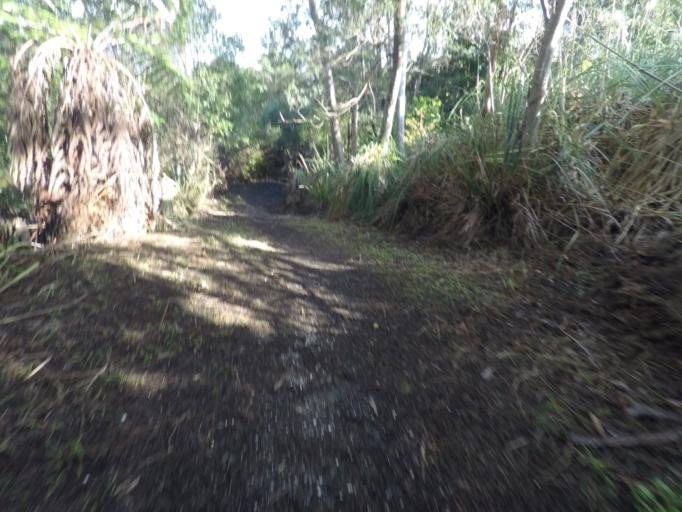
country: NZ
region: Auckland
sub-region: Auckland
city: Waitakere
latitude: -36.9020
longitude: 174.6429
